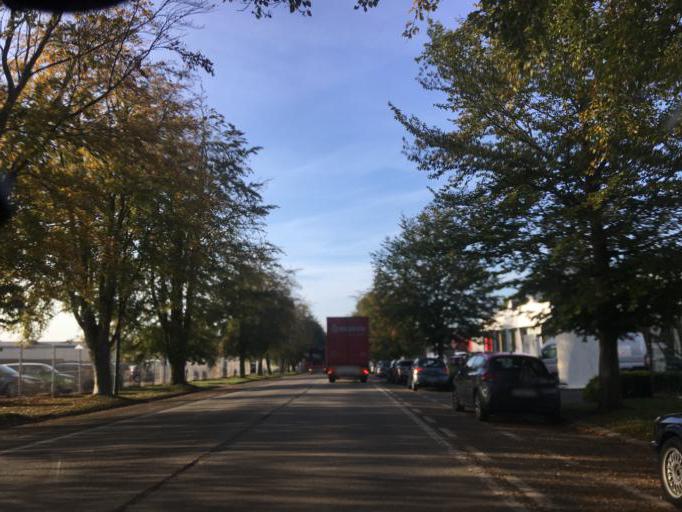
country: BE
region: Flanders
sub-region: Provincie West-Vlaanderen
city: Ieper
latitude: 50.8482
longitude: 2.9009
